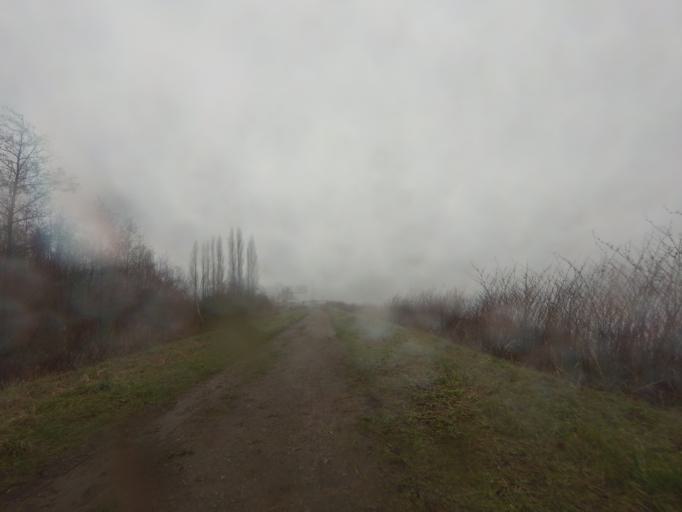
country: BE
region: Flanders
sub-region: Provincie Antwerpen
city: Hoboken
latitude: 51.1823
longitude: 4.3325
